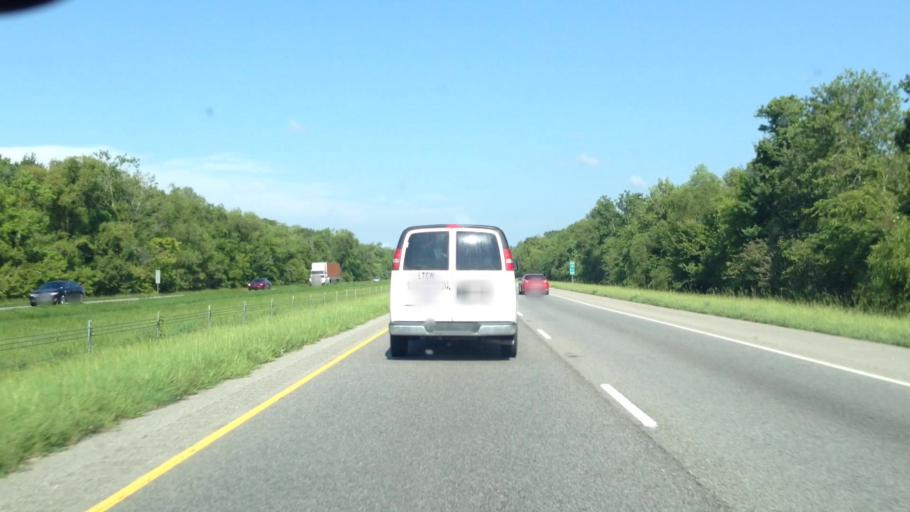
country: US
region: Louisiana
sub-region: Saint John the Baptist Parish
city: Garyville
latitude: 30.1159
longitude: -90.5968
